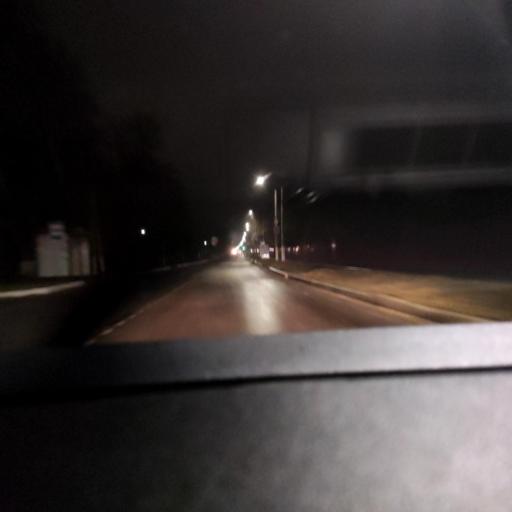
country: RU
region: Voronezj
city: Semiluki
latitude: 51.6918
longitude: 39.0350
